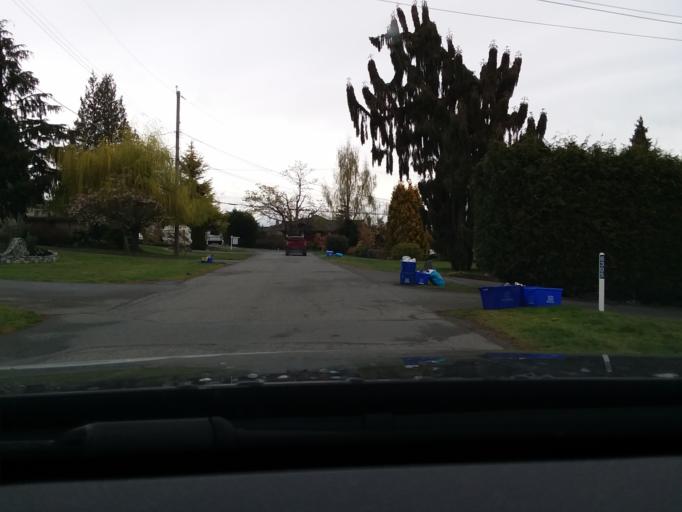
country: CA
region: British Columbia
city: North Saanich
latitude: 48.5535
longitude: -123.3954
